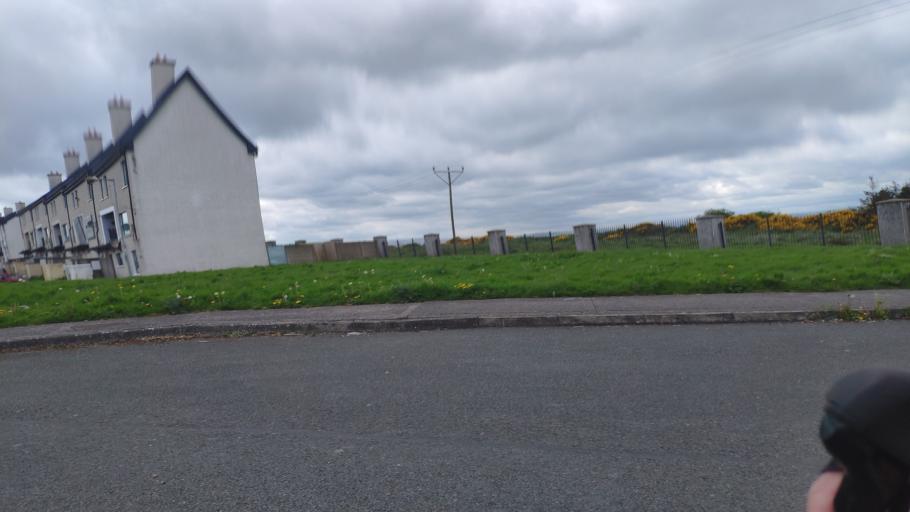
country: IE
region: Munster
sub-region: County Cork
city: Cork
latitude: 51.9132
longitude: -8.5005
